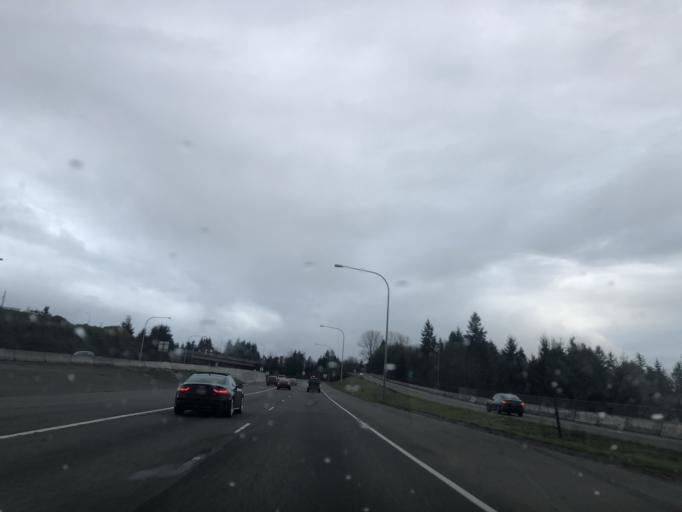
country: US
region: Washington
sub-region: Pierce County
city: University Place
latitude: 47.2607
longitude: -122.5415
